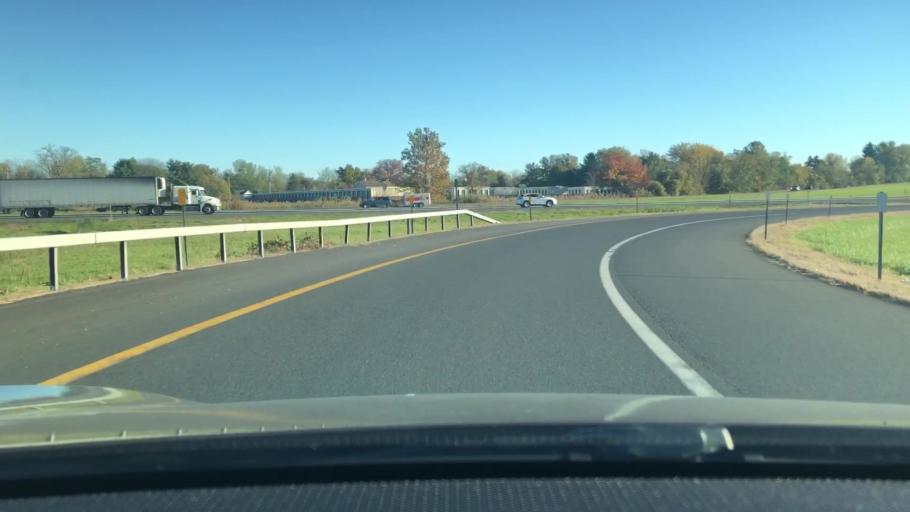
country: US
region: New York
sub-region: Ulster County
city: Lincoln Park
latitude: 41.9500
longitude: -74.0259
